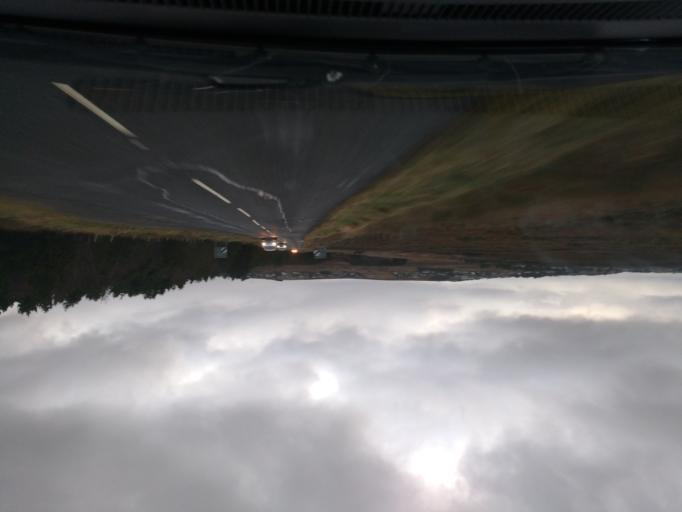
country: GB
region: Scotland
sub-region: Eilean Siar
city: Isle of Lewis
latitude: 58.2446
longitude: -6.3615
